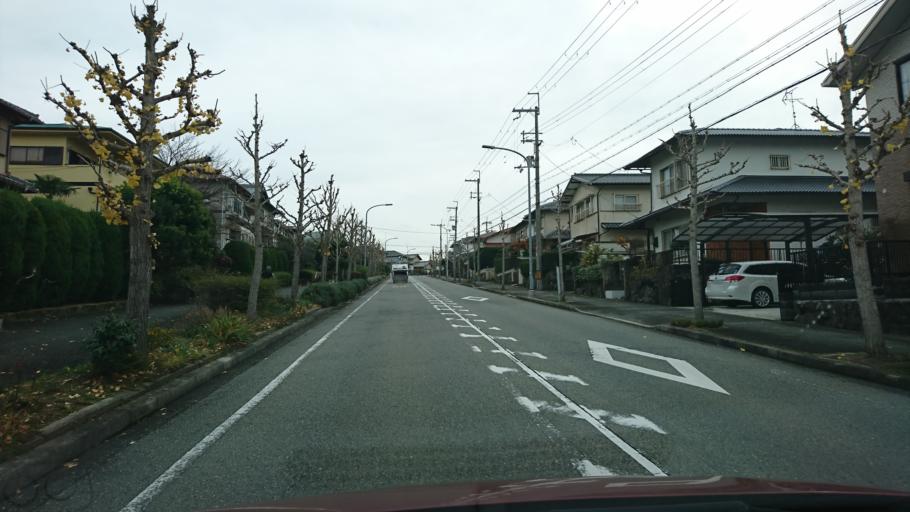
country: JP
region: Osaka
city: Mino
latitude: 34.8995
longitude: 135.4468
